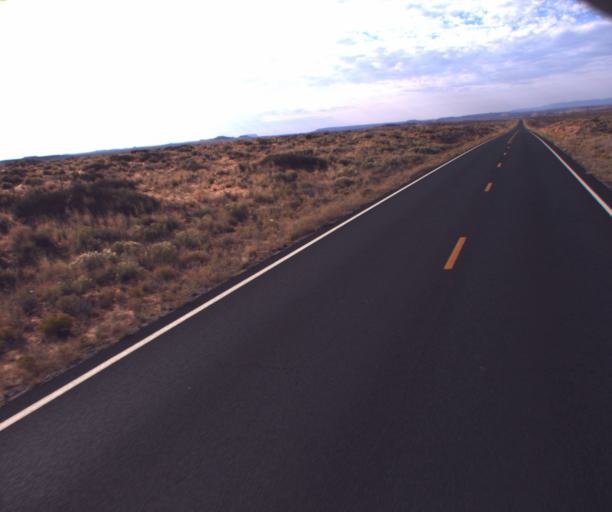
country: US
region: Arizona
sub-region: Apache County
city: Many Farms
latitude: 36.8567
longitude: -109.6366
